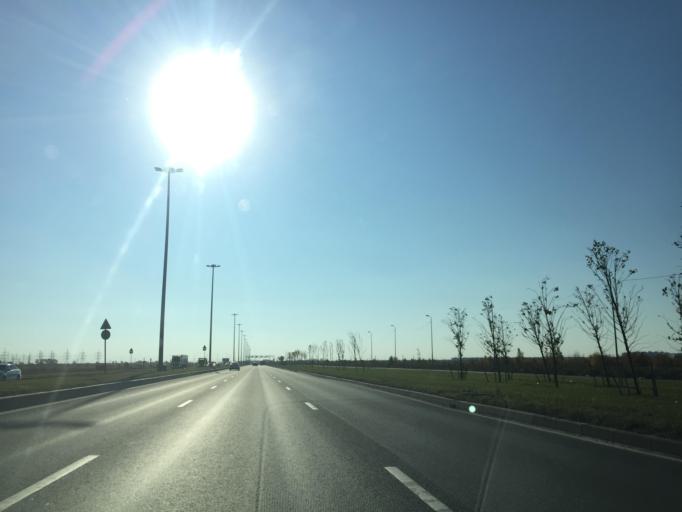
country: RU
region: St.-Petersburg
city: Petro-Slavyanka
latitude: 59.7766
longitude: 30.4984
